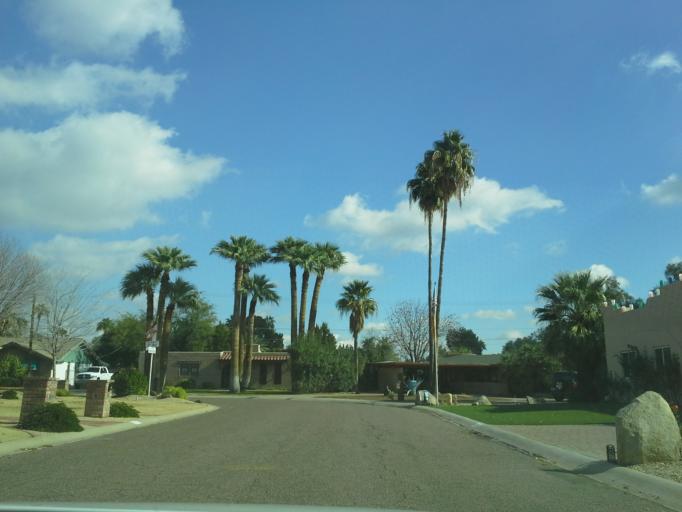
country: US
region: Arizona
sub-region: Maricopa County
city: Glendale
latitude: 33.6188
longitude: -112.0750
